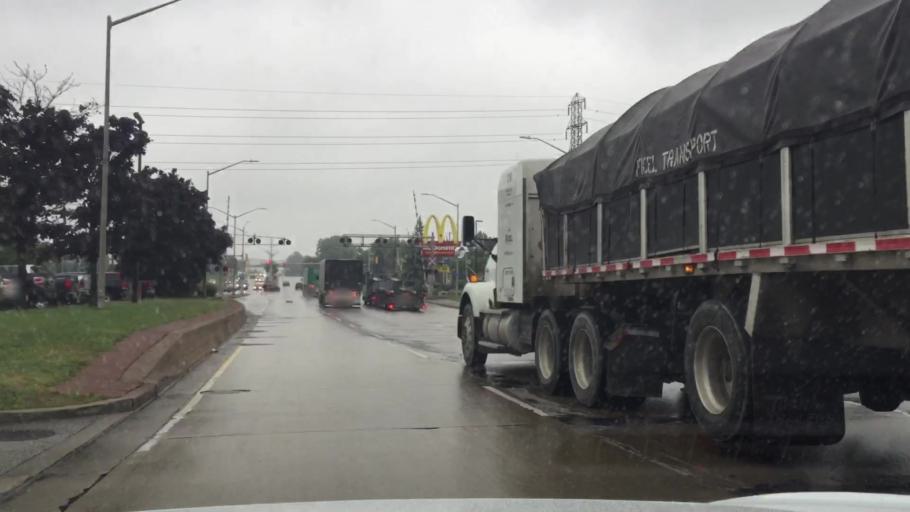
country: US
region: Michigan
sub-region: Wayne County
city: Detroit
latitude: 42.2999
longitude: -83.0659
